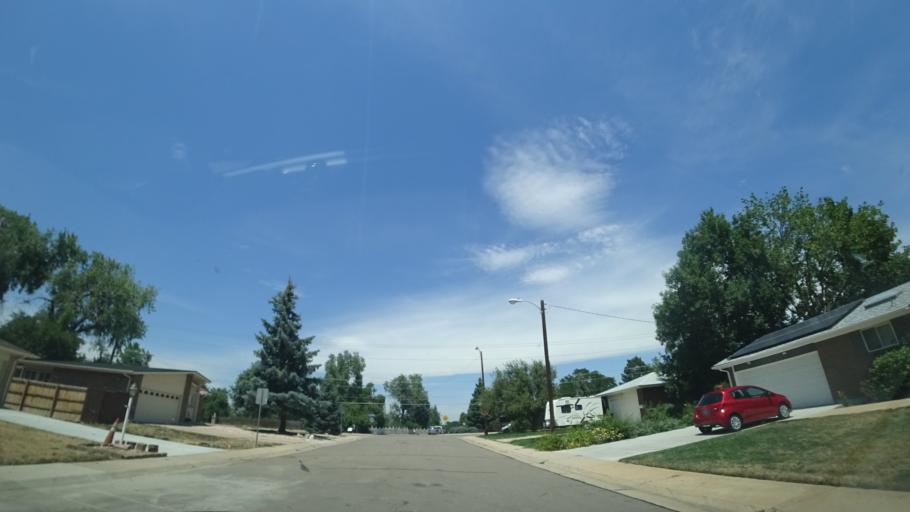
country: US
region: Colorado
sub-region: Jefferson County
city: Lakewood
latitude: 39.6960
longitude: -105.0905
